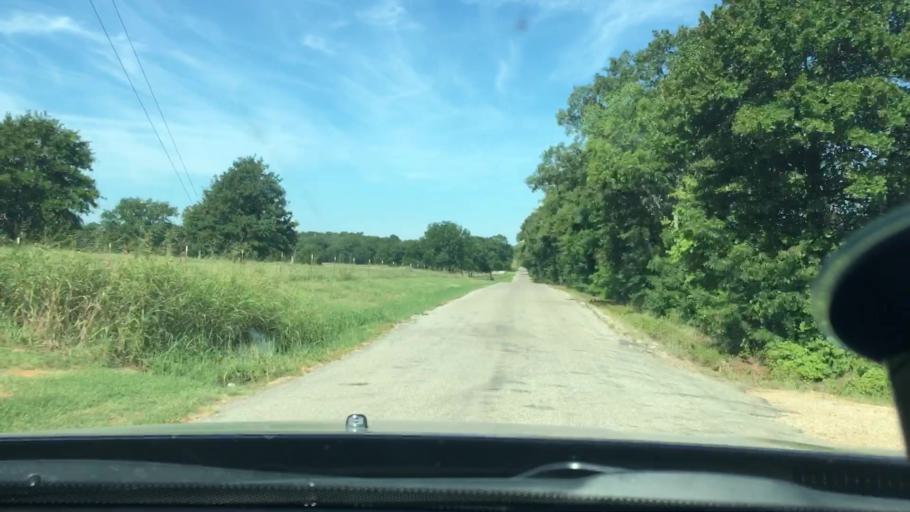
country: US
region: Oklahoma
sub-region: Carter County
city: Lone Grove
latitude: 34.2674
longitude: -97.2648
